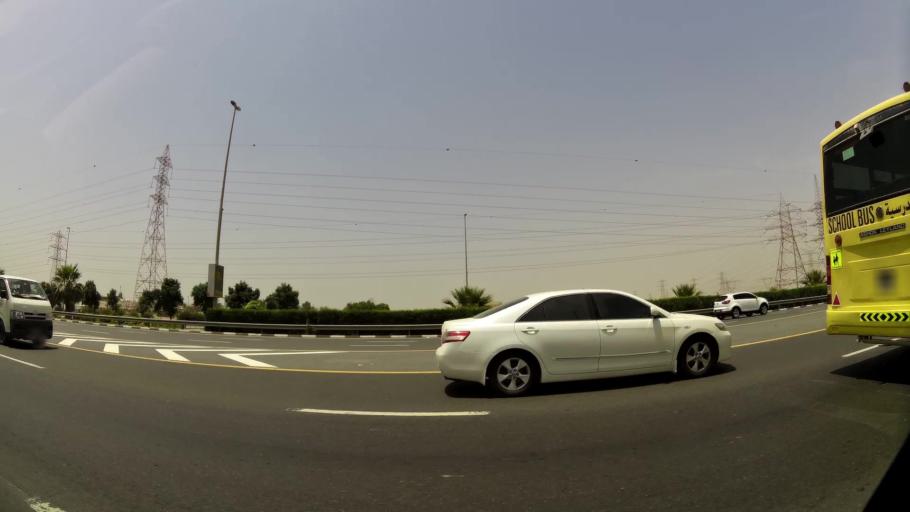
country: AE
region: Ash Shariqah
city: Sharjah
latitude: 25.2120
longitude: 55.3976
